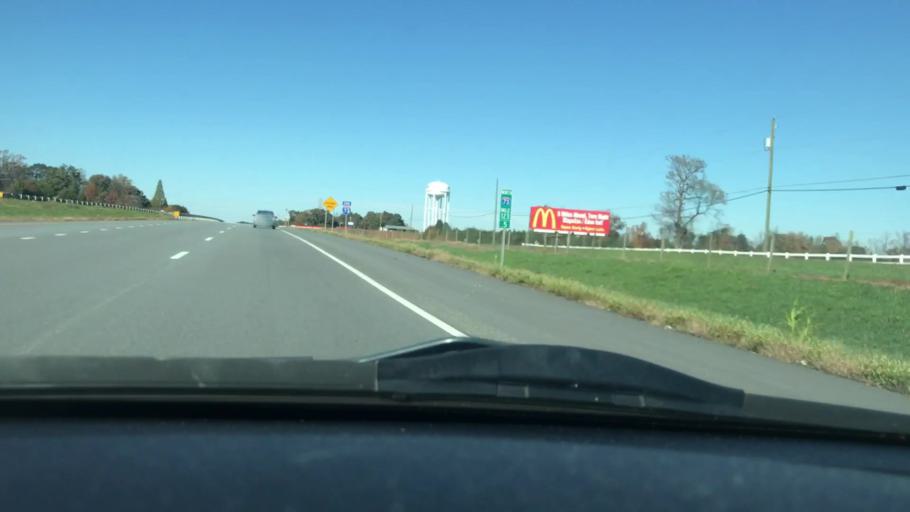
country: US
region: North Carolina
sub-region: Guilford County
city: Stokesdale
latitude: 36.2892
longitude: -79.9397
